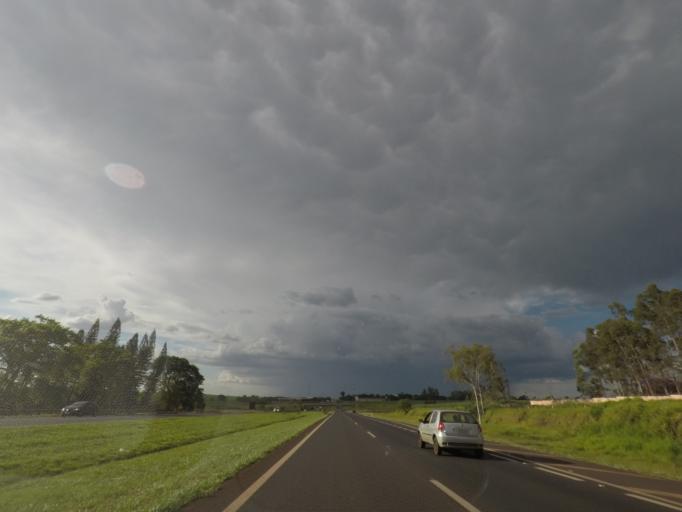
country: BR
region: Sao Paulo
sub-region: Jardinopolis
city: Jardinopolis
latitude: -21.0541
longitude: -47.8233
